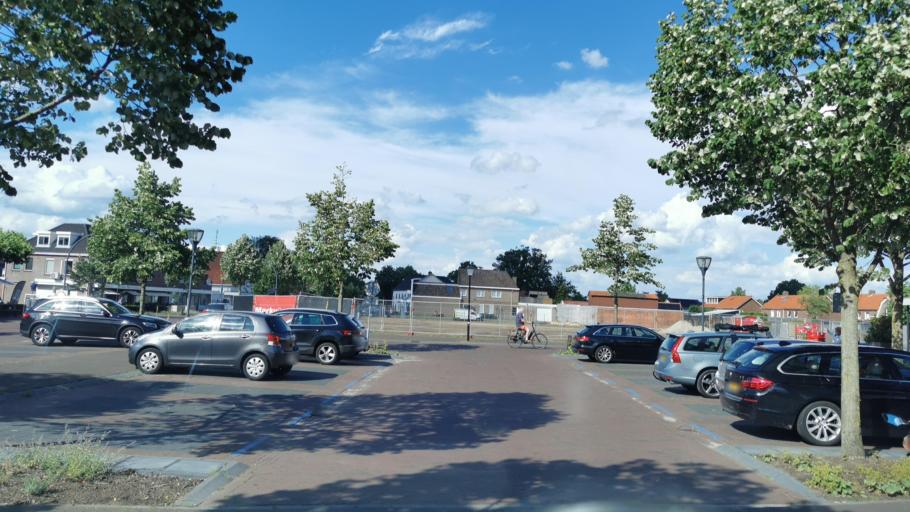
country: DE
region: Lower Saxony
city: Nordhorn
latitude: 52.3755
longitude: 7.0064
